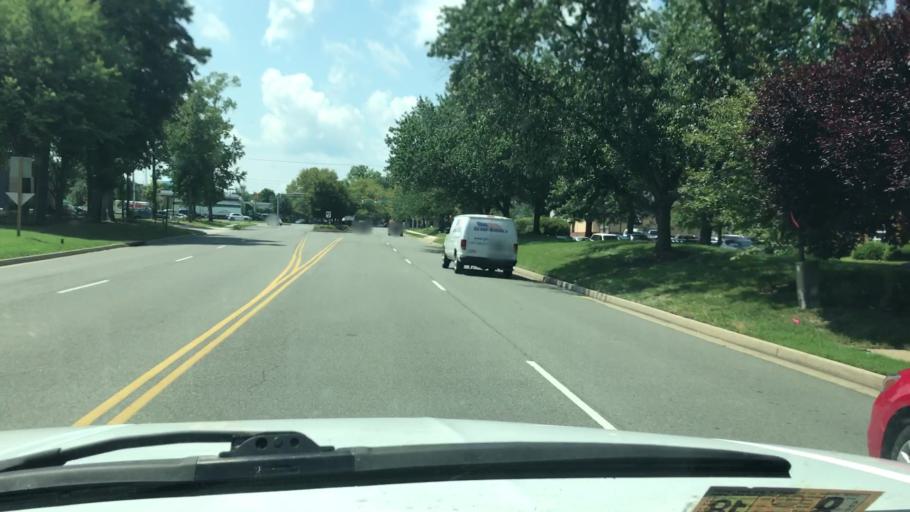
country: US
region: Virginia
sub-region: Henrico County
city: Short Pump
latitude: 37.6490
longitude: -77.5861
